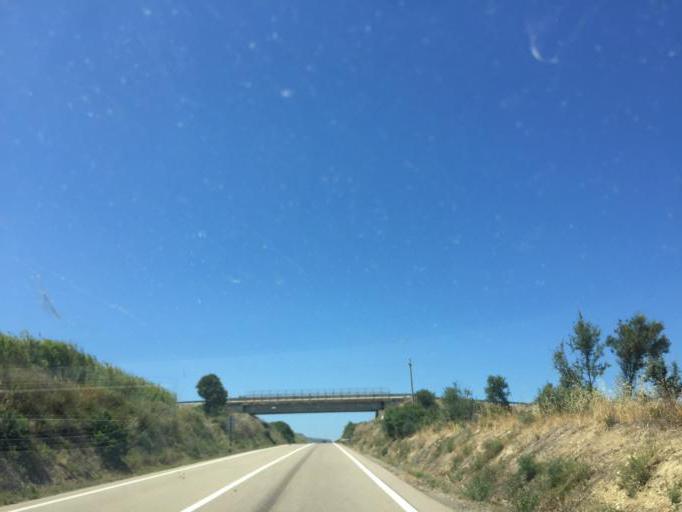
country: IT
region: Sardinia
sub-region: Provincia di Sassari
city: Codaruina
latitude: 40.9175
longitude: 8.8356
